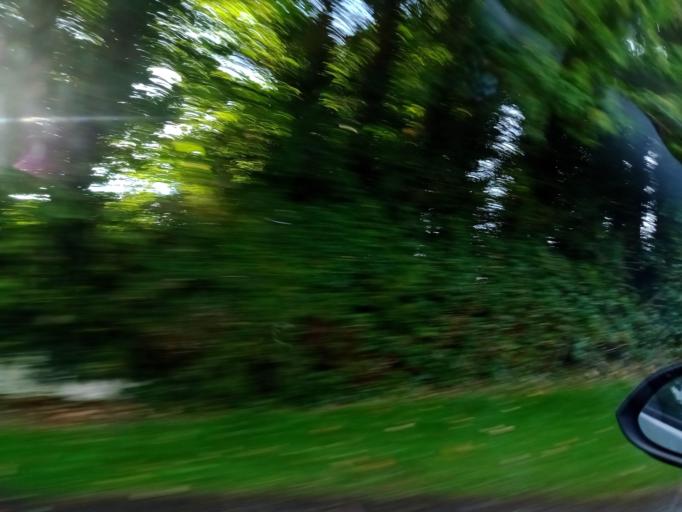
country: IE
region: Leinster
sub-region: Laois
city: Stradbally
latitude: 53.0039
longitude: -7.2123
